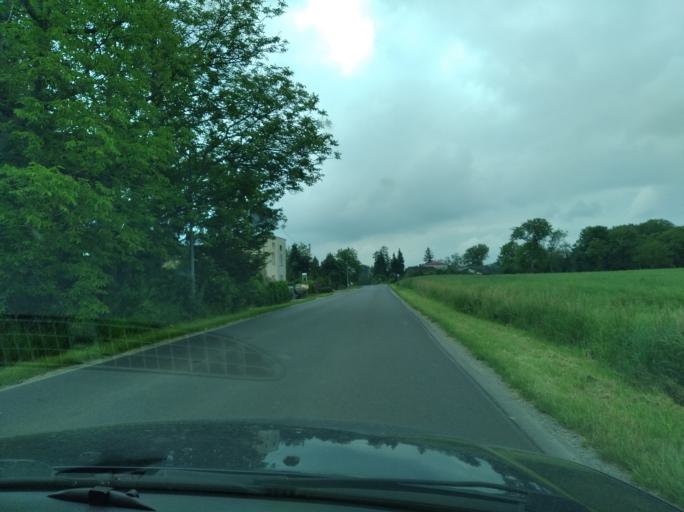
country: PL
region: Subcarpathian Voivodeship
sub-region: Powiat jaroslawski
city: Pawlosiow
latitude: 50.0197
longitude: 22.6401
